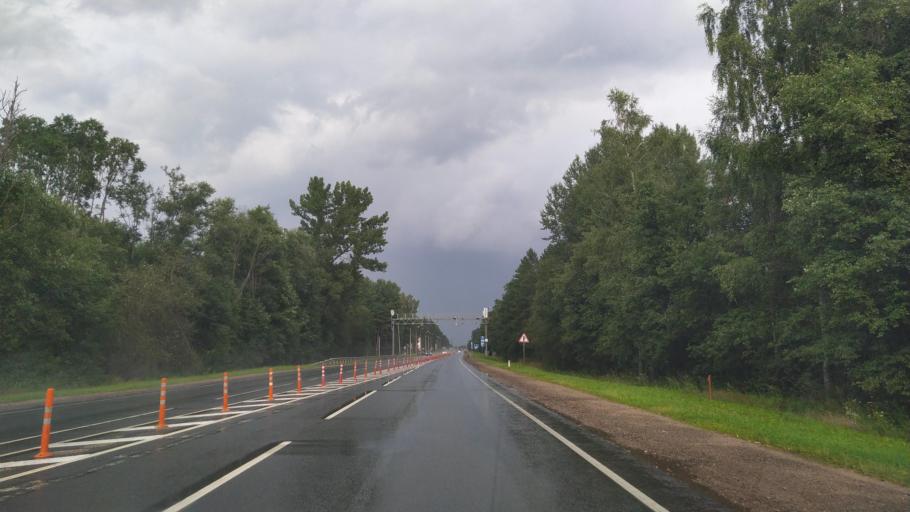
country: RU
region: Pskov
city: Pskov
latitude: 57.7301
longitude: 28.3570
